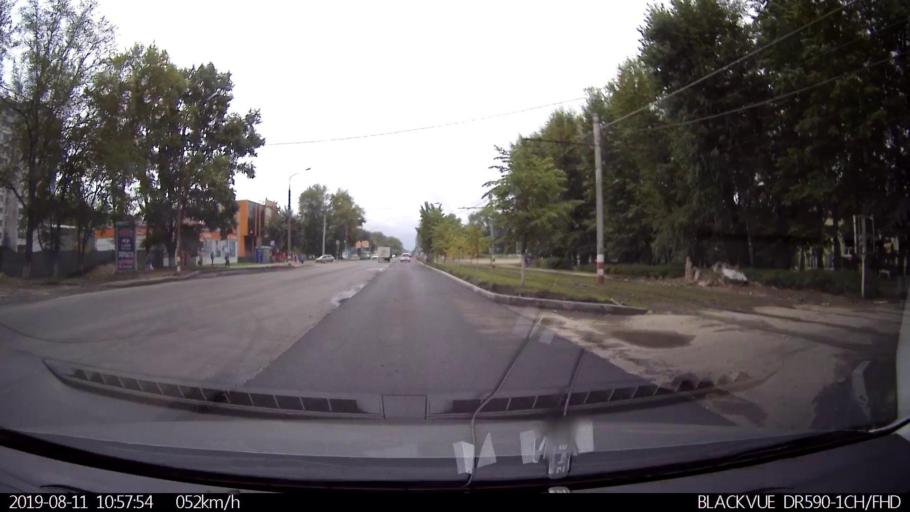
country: RU
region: Ulyanovsk
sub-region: Ulyanovskiy Rayon
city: Ulyanovsk
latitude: 54.2556
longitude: 48.3196
